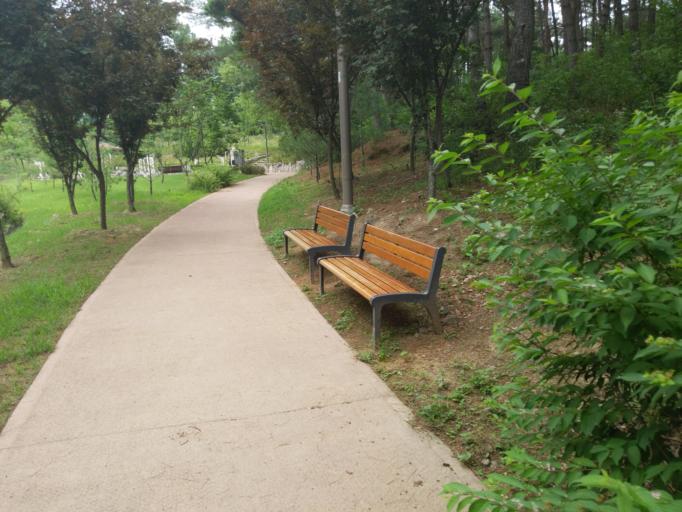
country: KR
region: Daegu
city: Hwawon
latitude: 35.8030
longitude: 128.5332
